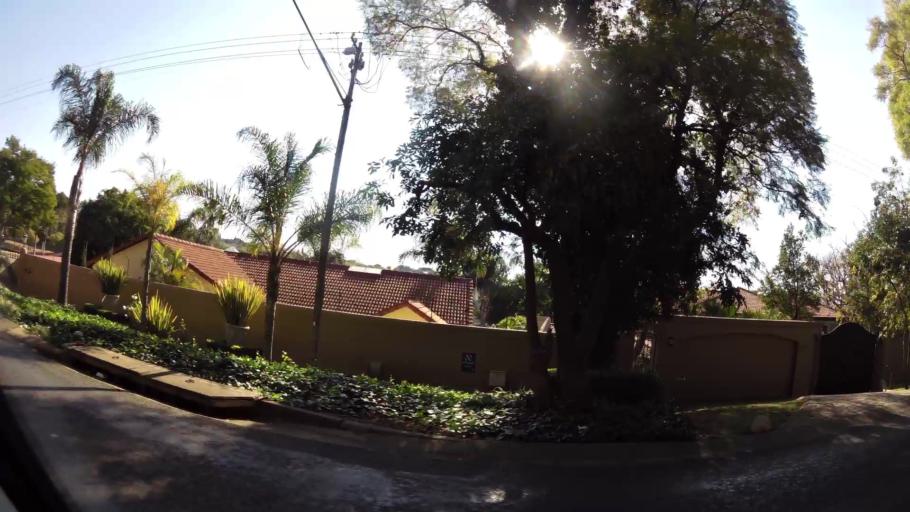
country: ZA
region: Gauteng
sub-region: City of Tshwane Metropolitan Municipality
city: Pretoria
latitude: -25.7920
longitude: 28.2447
